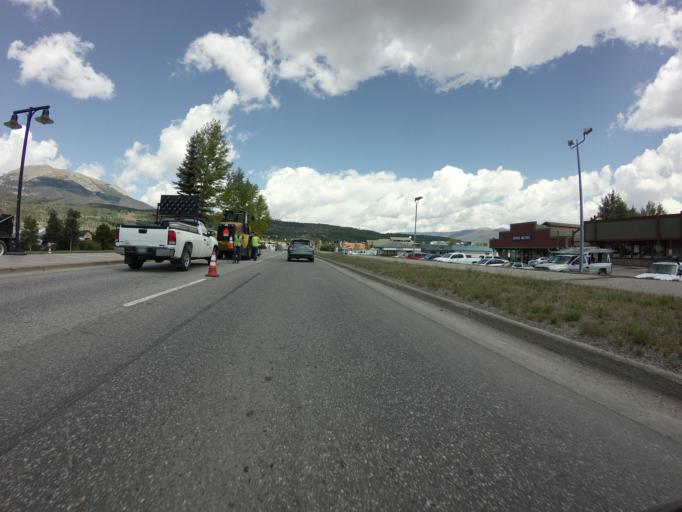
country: US
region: Colorado
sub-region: Summit County
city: Frisco
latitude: 39.5865
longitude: -106.0945
